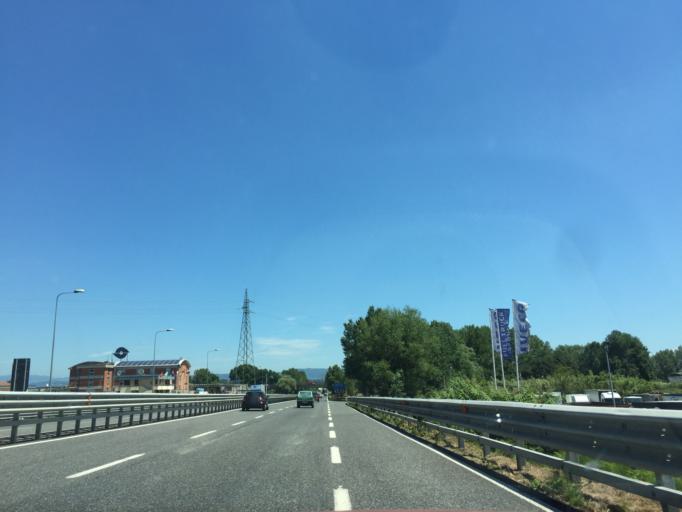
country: IT
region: Tuscany
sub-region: Province of Pisa
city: San Miniato
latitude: 43.6921
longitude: 10.7859
